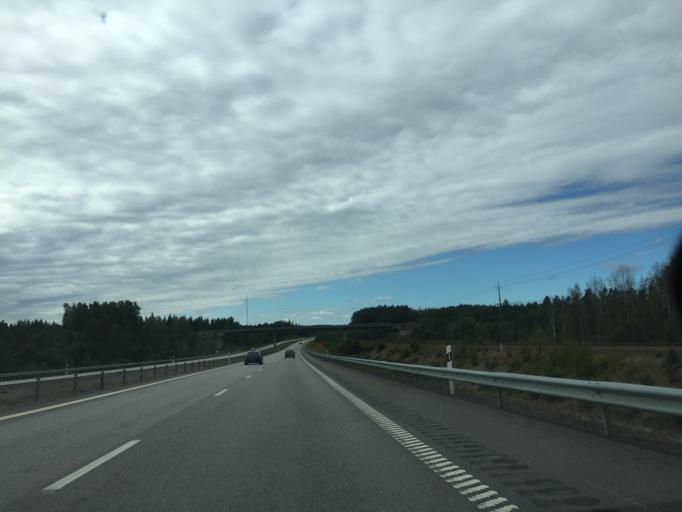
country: SE
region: OErebro
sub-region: Lindesbergs Kommun
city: Fellingsbro
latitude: 59.3826
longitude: 15.6608
